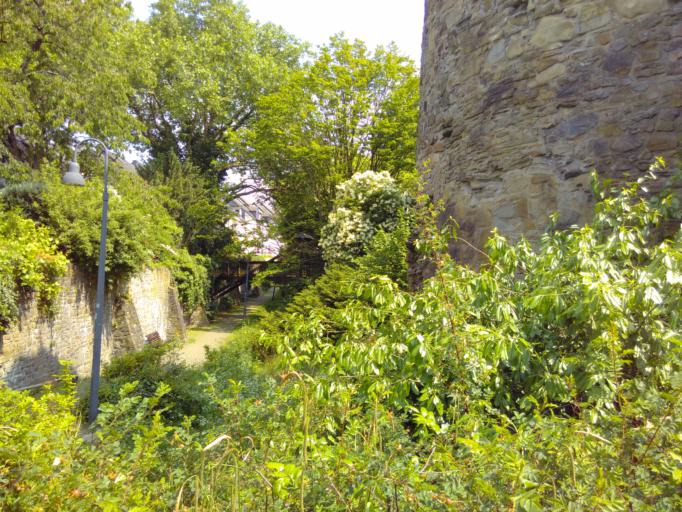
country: DE
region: North Rhine-Westphalia
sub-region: Regierungsbezirk Dusseldorf
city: Ratingen
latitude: 51.2989
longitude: 6.8503
